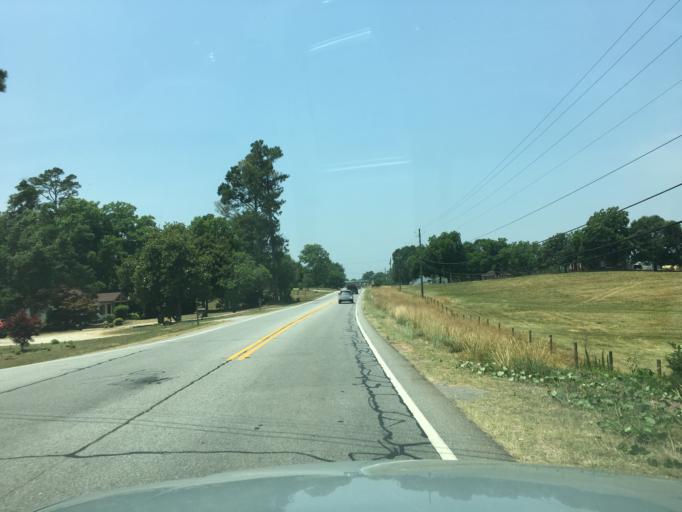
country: US
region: Georgia
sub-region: Hart County
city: Royston
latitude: 34.2846
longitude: -83.1536
